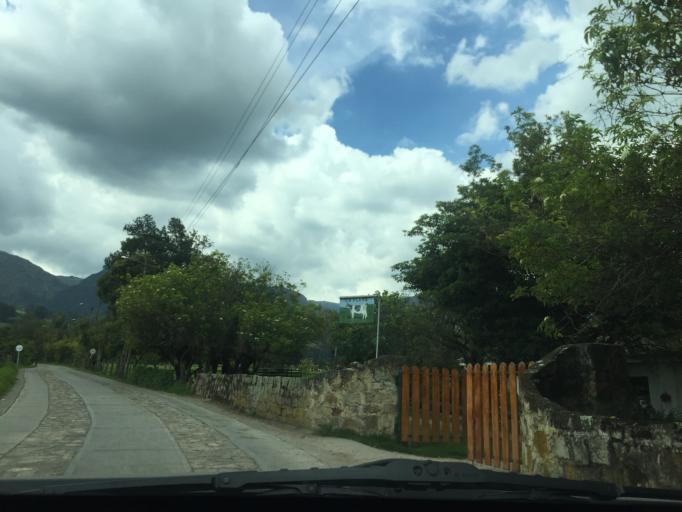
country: CO
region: Cundinamarca
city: Cogua
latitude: 5.0512
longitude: -73.9897
